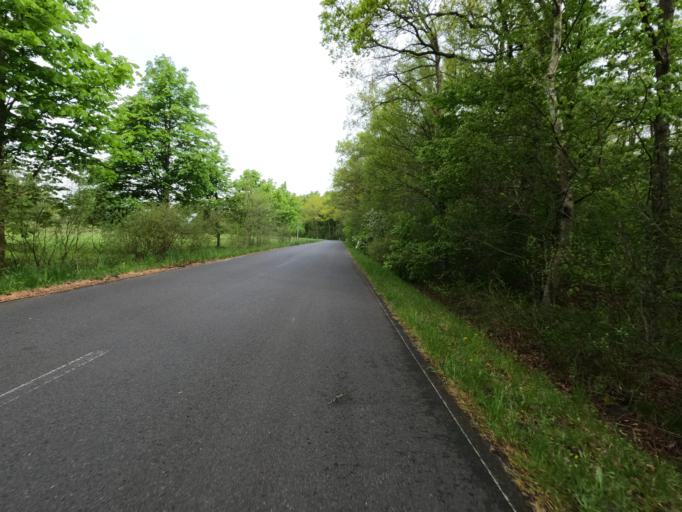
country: DE
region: Mecklenburg-Vorpommern
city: Born
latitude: 54.3497
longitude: 12.5745
